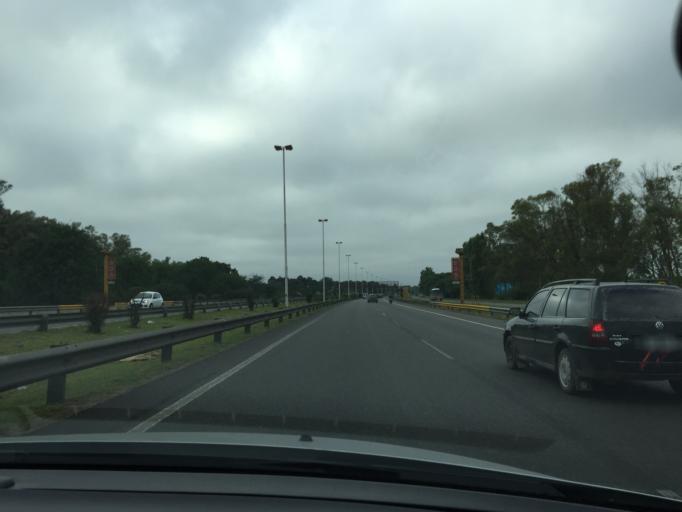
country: AR
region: Buenos Aires
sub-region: Partido de Ezeiza
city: Ezeiza
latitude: -34.7932
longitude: -58.5163
